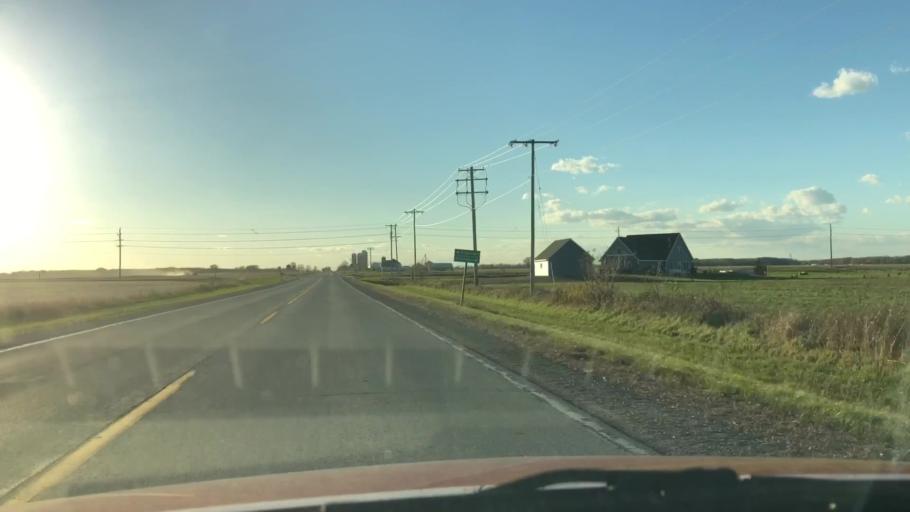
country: US
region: Wisconsin
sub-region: Outagamie County
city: Seymour
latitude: 44.4439
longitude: -88.2887
